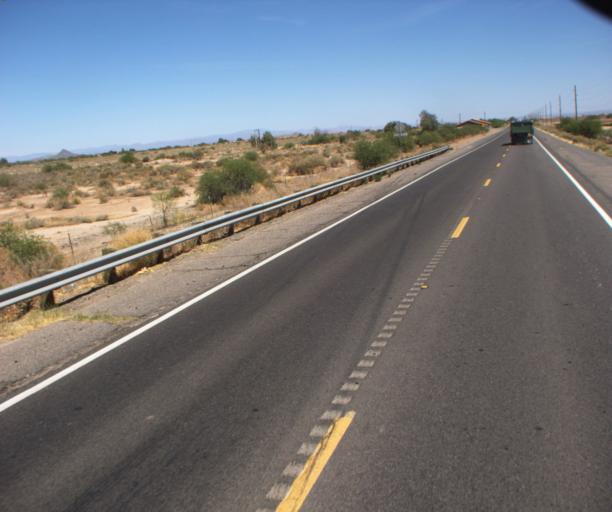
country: US
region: Arizona
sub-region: Pinal County
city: Blackwater
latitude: 33.0025
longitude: -111.5995
